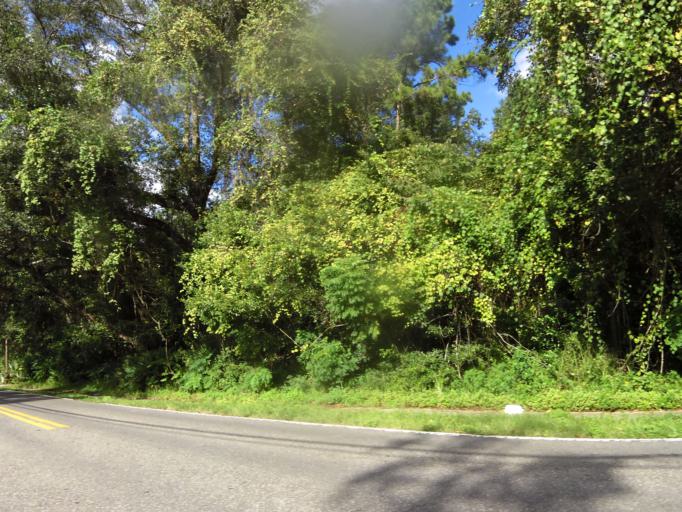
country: US
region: Florida
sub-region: Duval County
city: Jacksonville
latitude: 30.2891
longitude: -81.7389
